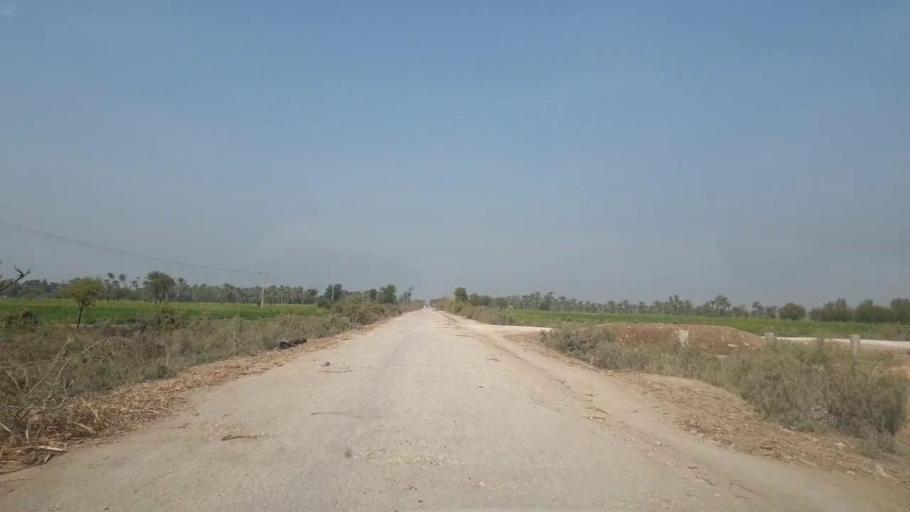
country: PK
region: Sindh
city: Mirpur Khas
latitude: 25.6803
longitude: 69.1551
